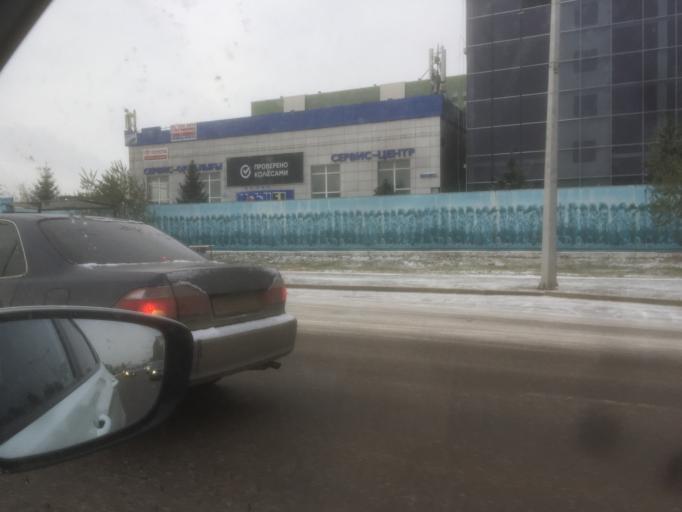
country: KZ
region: Astana Qalasy
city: Astana
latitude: 51.1471
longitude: 71.4591
